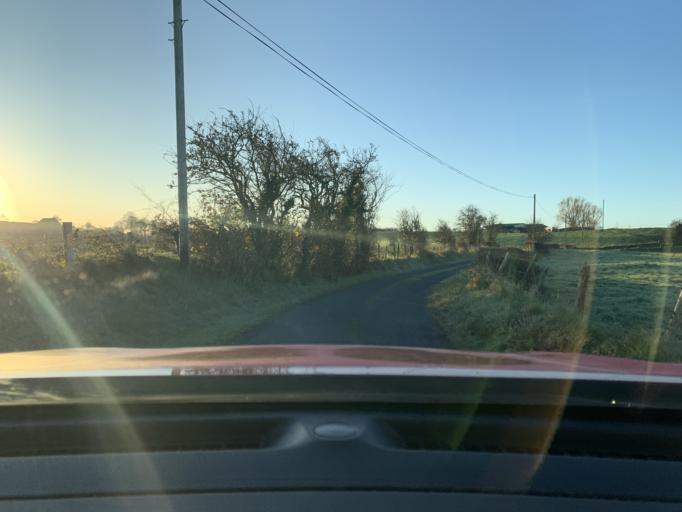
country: IE
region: Connaught
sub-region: Sligo
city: Ballymote
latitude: 54.0703
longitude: -8.5495
